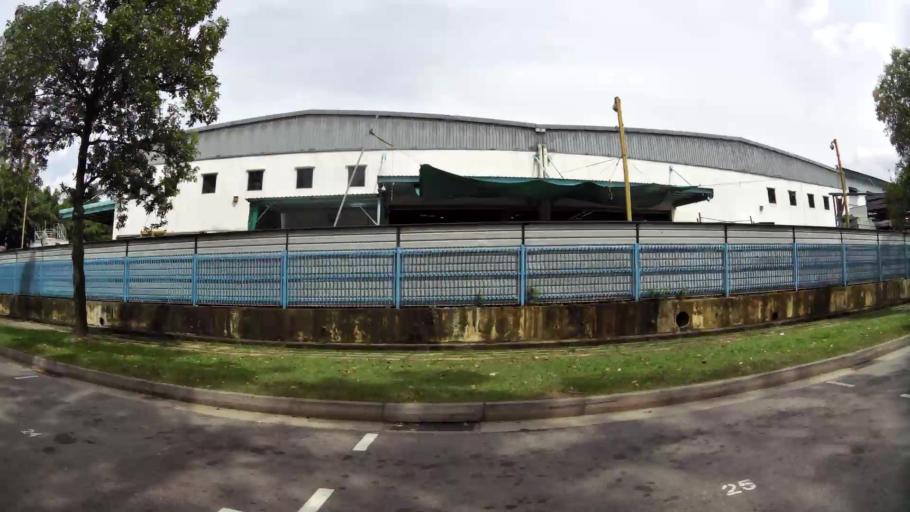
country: MY
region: Johor
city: Johor Bahru
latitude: 1.4193
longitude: 103.7428
